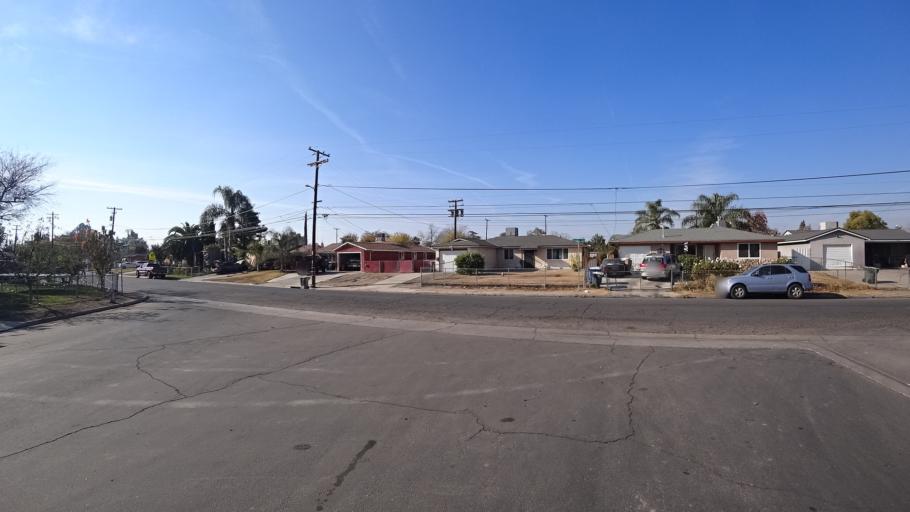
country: US
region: California
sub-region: Kern County
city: Bakersfield
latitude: 35.3258
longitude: -119.0158
